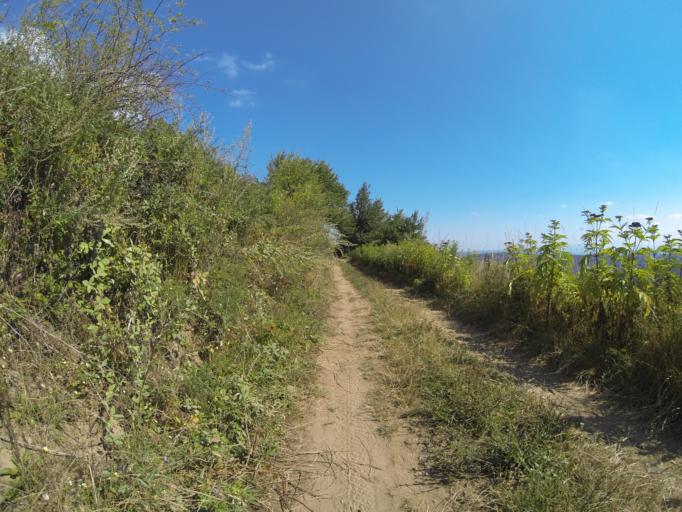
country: RO
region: Mehedinti
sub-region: Comuna Svinita
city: Svinita
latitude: 44.5633
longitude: 22.1392
